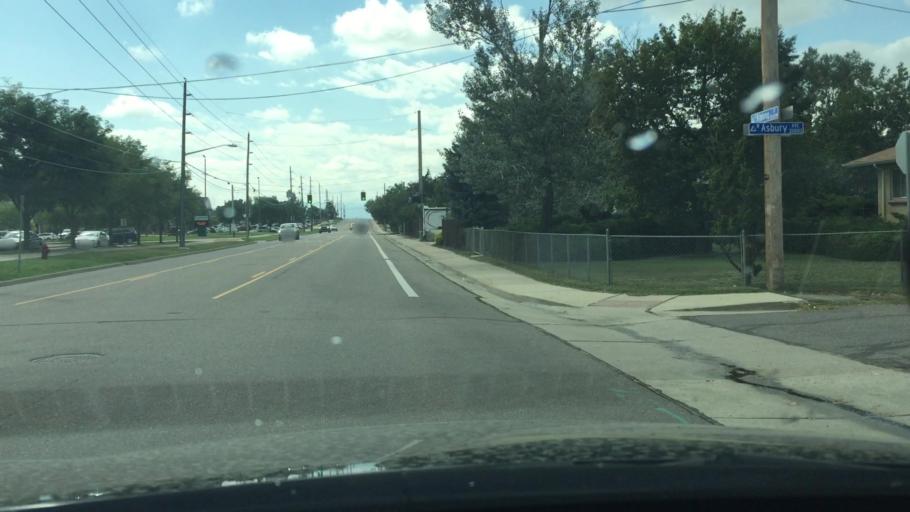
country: US
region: Colorado
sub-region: Jefferson County
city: Lakewood
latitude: 39.6802
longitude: -105.1097
